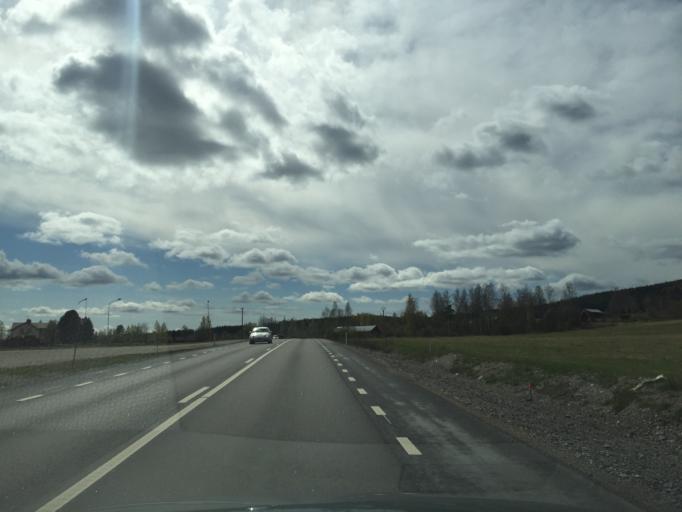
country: SE
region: Gaevleborg
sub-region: Bollnas Kommun
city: Arbra
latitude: 61.5053
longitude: 16.3575
